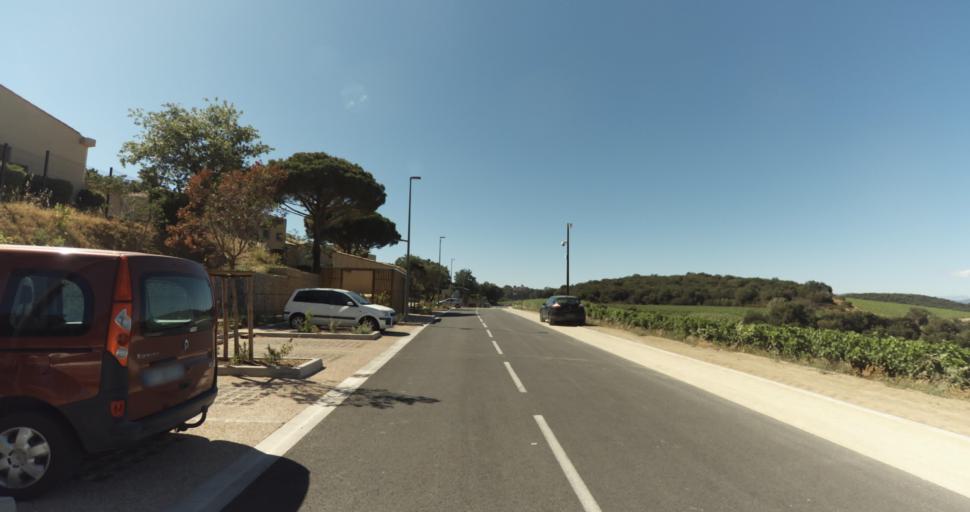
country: FR
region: Provence-Alpes-Cote d'Azur
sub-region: Departement du Var
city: La Croix-Valmer
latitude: 43.2127
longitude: 6.5620
